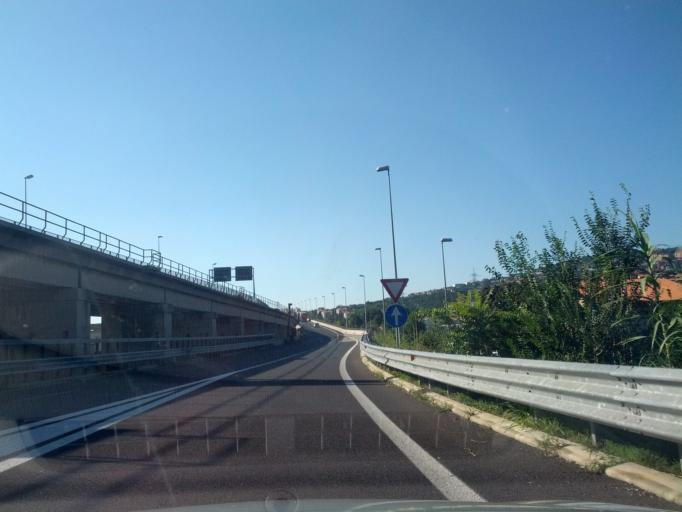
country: IT
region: Friuli Venezia Giulia
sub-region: Provincia di Trieste
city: Domio
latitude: 45.6103
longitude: 13.8292
